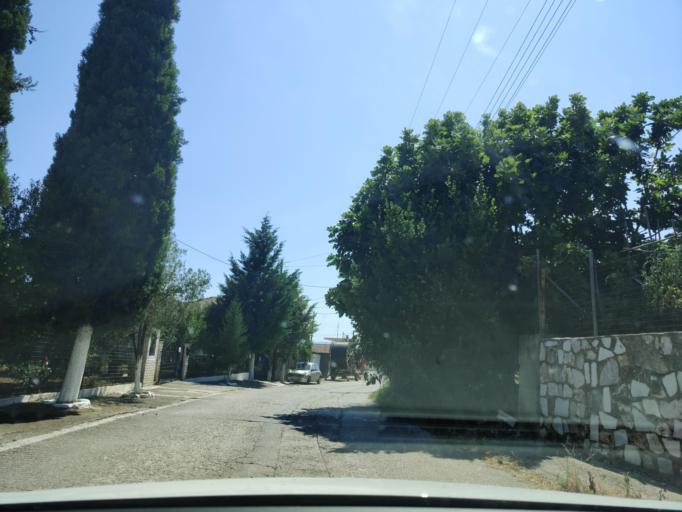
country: GR
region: East Macedonia and Thrace
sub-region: Nomos Kavalas
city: Zygos
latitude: 41.0153
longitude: 24.3810
